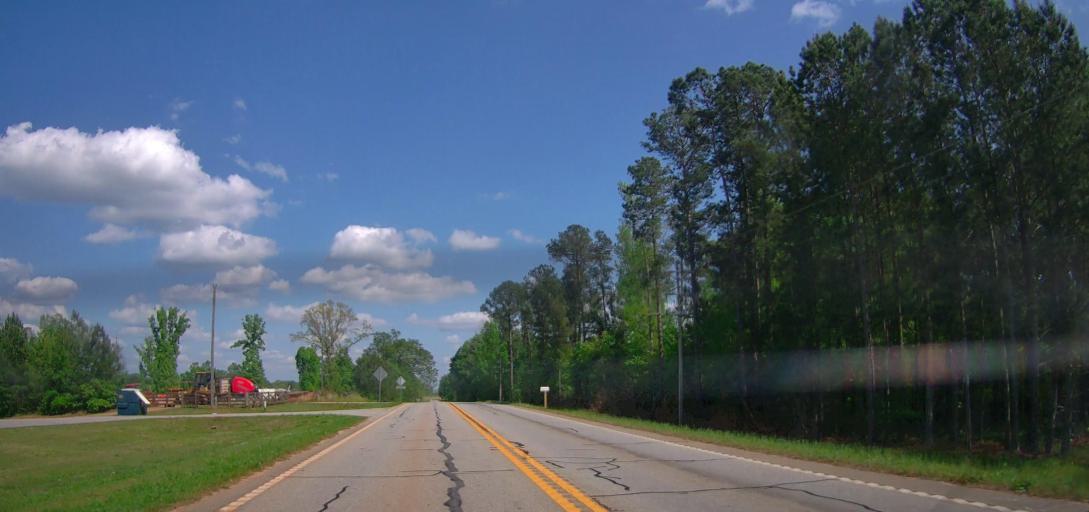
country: US
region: Georgia
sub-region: Greene County
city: Greensboro
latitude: 33.6159
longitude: -83.3225
